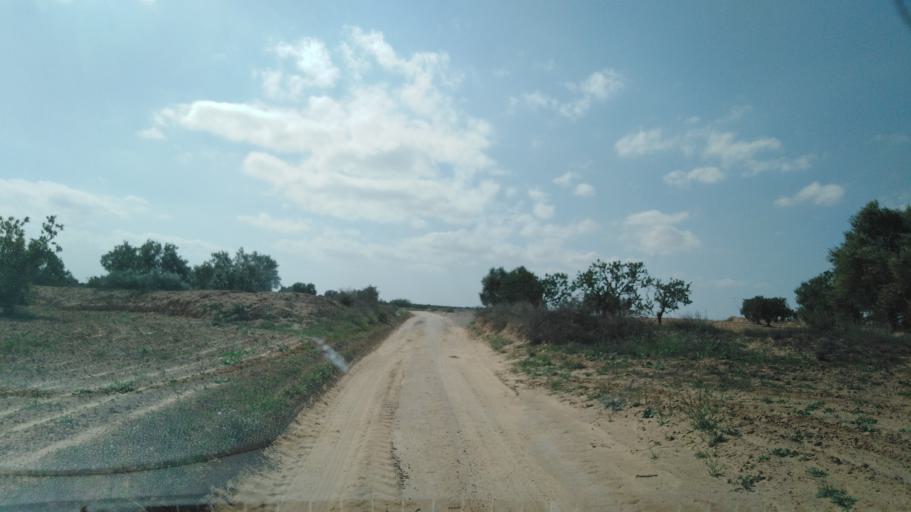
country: TN
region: Safaqis
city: Bi'r `Ali Bin Khalifah
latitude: 34.7999
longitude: 10.3820
